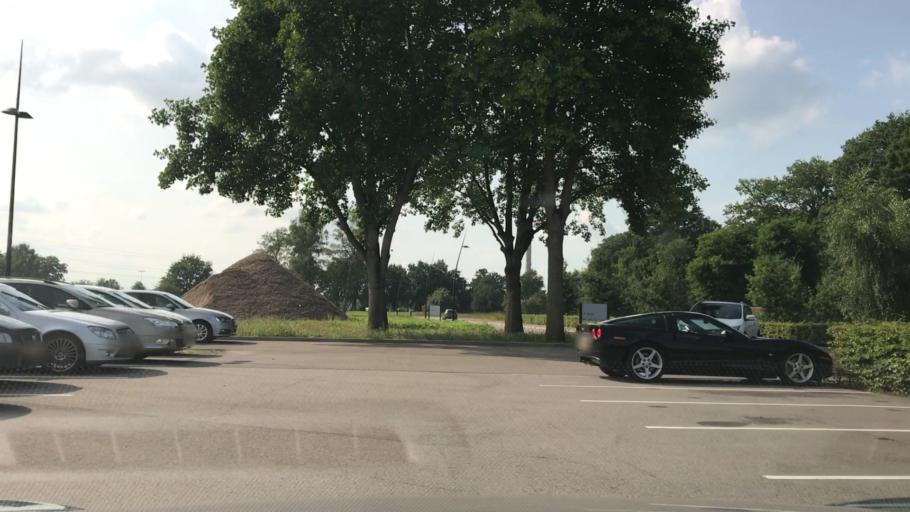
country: NL
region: Overijssel
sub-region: Gemeente Hengelo
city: Hengelo
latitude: 52.2462
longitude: 6.7696
